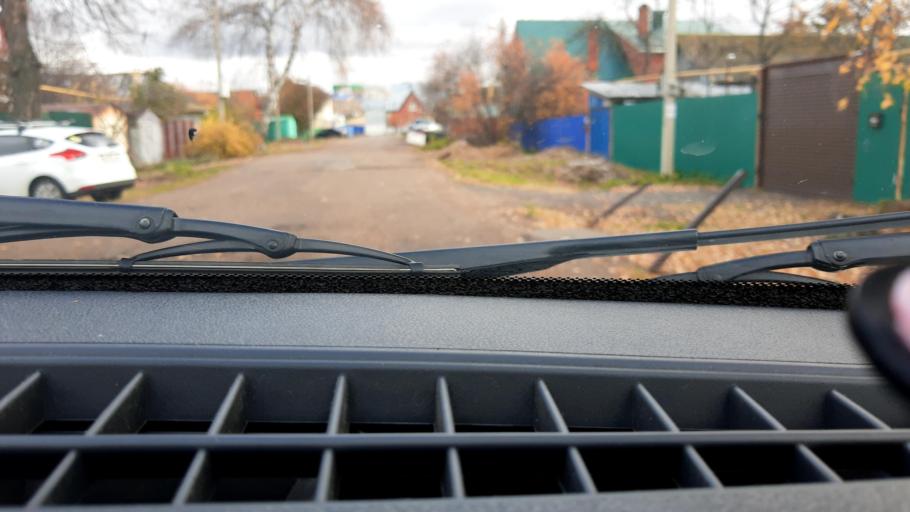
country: RU
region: Bashkortostan
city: Ufa
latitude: 54.7791
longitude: 56.0610
